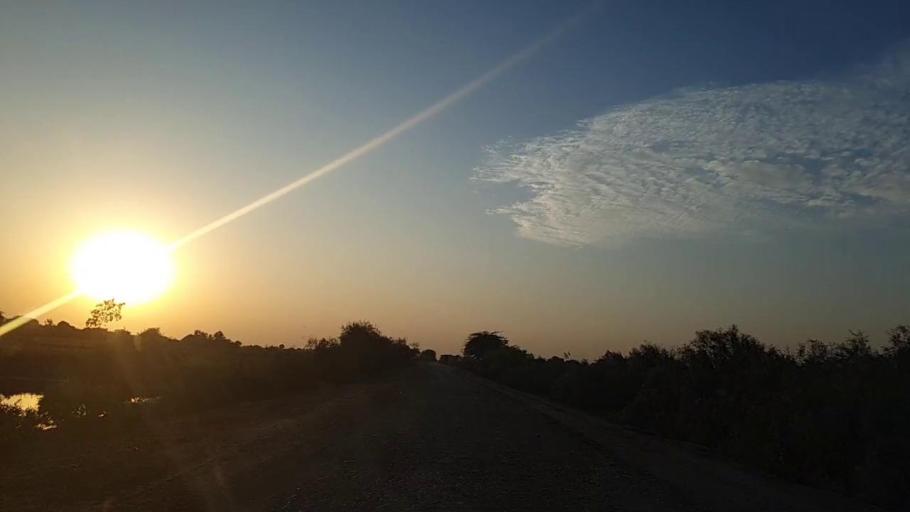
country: PK
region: Sindh
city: Chuhar Jamali
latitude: 24.4612
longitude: 68.1128
